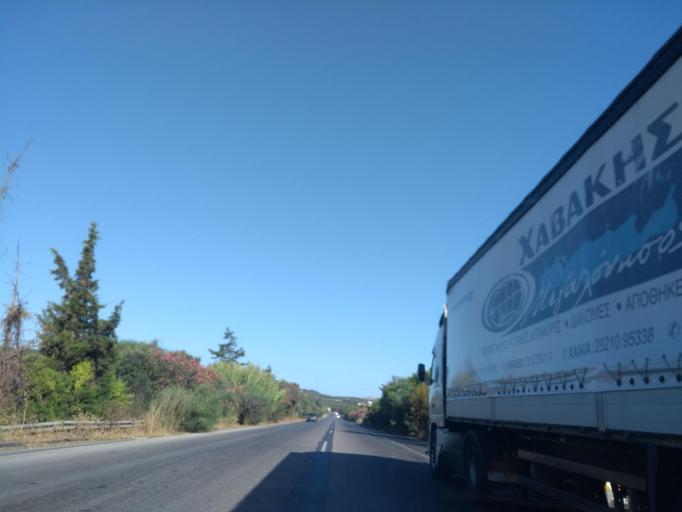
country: GR
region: Crete
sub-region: Nomos Chanias
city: Gerani
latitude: 35.5152
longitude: 23.8487
